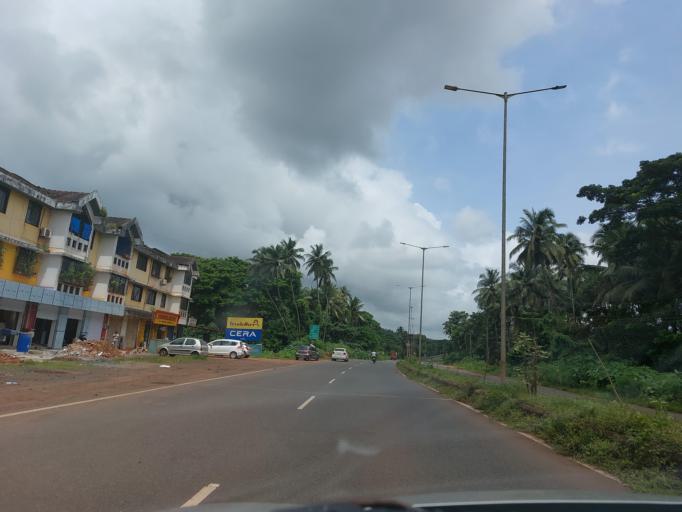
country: IN
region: Goa
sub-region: North Goa
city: Queula
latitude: 15.3883
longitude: 73.9980
